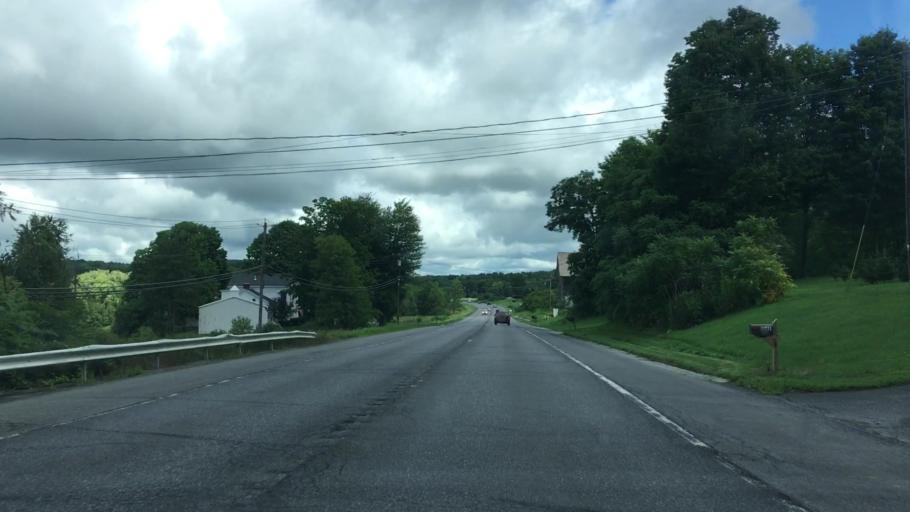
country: US
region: New York
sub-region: Rensselaer County
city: Poestenkill
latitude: 42.7808
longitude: -73.5810
